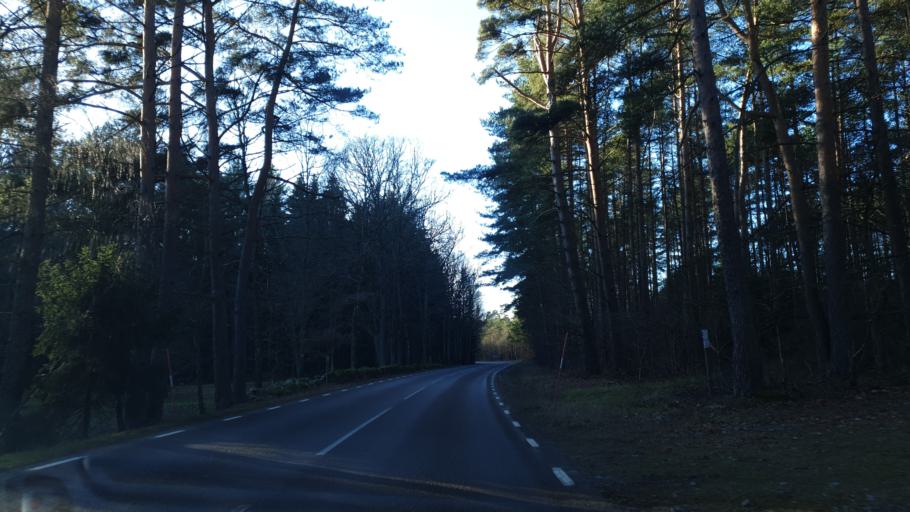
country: SE
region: Blekinge
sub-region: Ronneby Kommun
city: Kallinge
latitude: 56.2168
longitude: 15.3972
